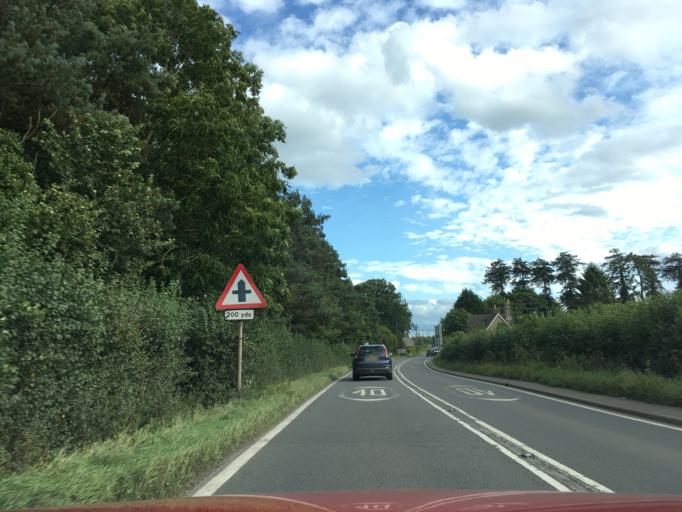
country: GB
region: England
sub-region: South Gloucestershire
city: Falfield
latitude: 51.6339
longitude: -2.4333
